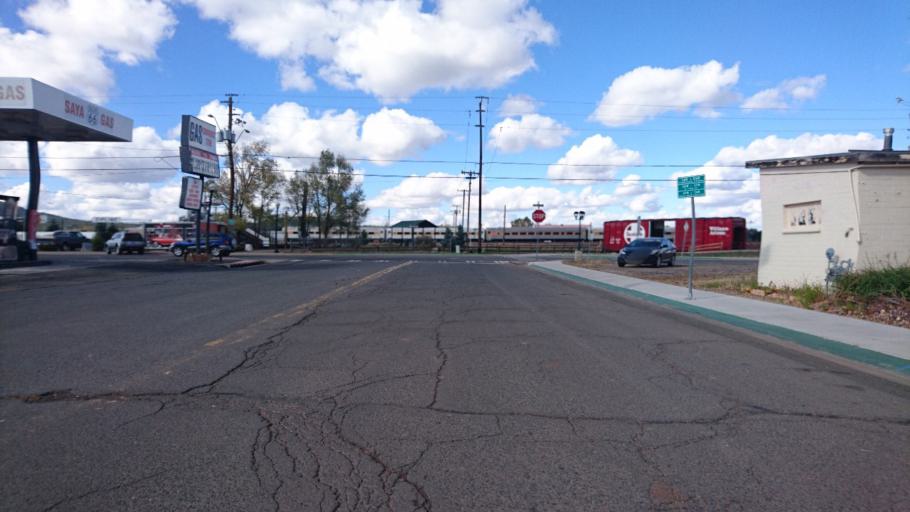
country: US
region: Arizona
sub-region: Coconino County
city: Williams
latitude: 35.2510
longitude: -112.1874
